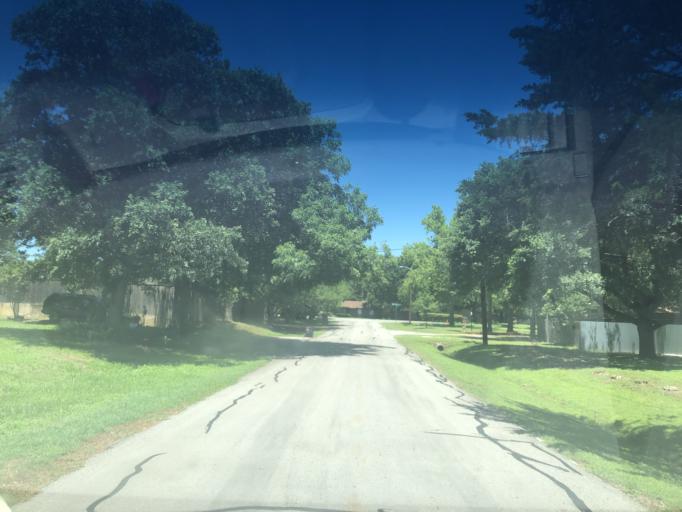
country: US
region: Texas
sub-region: Dallas County
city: Grand Prairie
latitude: 32.7758
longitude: -97.0329
